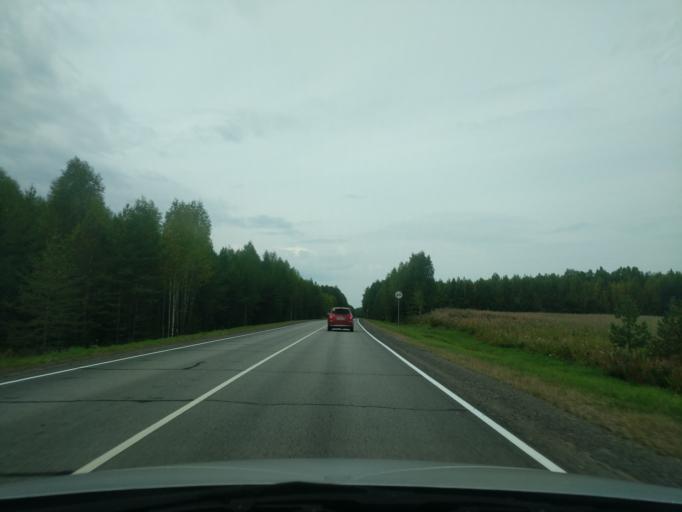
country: RU
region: Kirov
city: Kotel'nich
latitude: 58.2709
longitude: 48.0971
